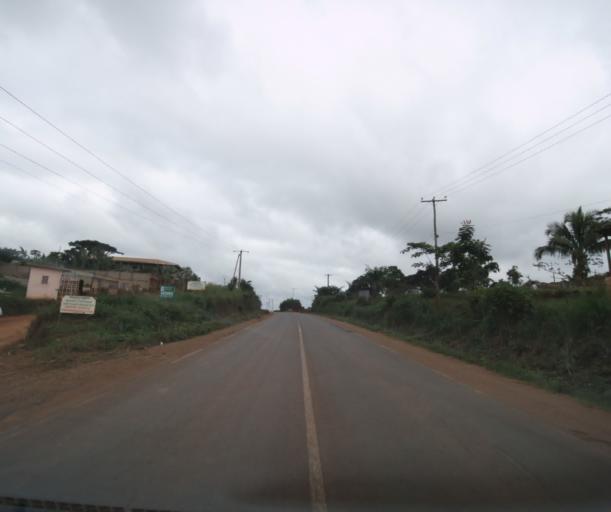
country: CM
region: Centre
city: Yaounde
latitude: 3.7949
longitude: 11.4793
